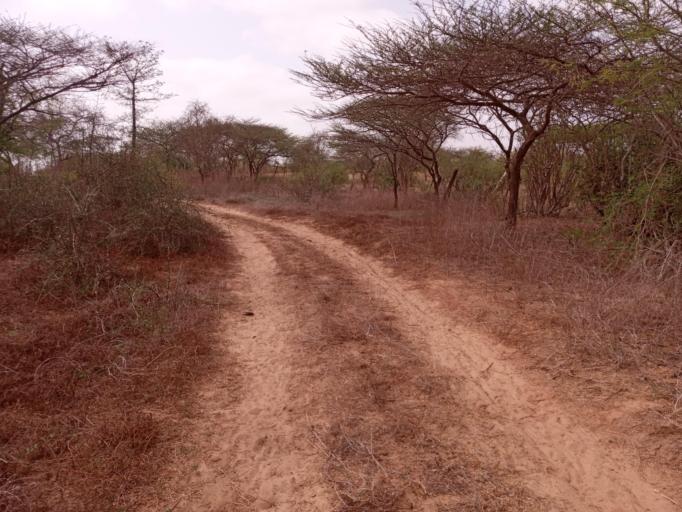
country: SN
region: Saint-Louis
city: Saint-Louis
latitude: 15.9221
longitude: -16.4527
